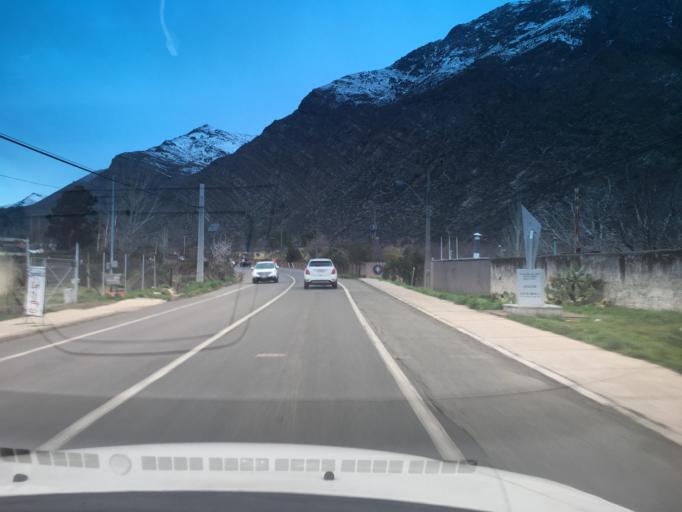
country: CL
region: Santiago Metropolitan
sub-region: Provincia de Cordillera
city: Puente Alto
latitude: -33.7179
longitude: -70.3310
